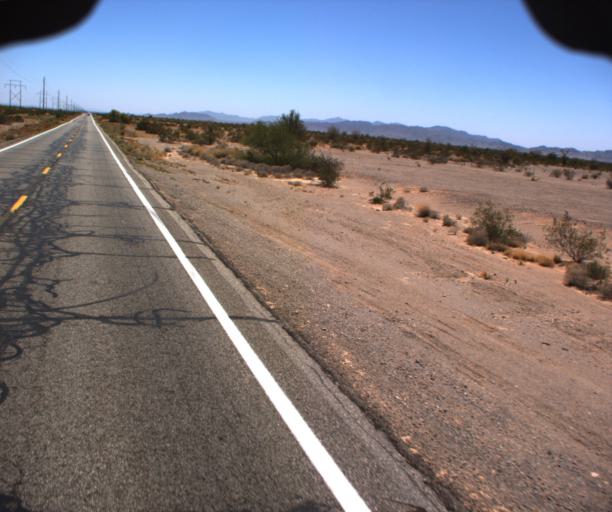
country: US
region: Arizona
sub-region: La Paz County
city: Quartzsite
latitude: 33.8389
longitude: -114.2170
